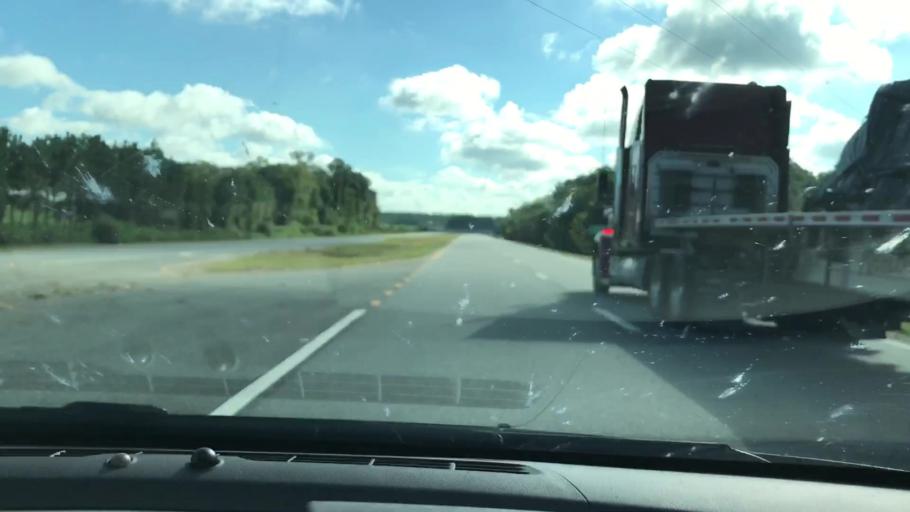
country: US
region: Georgia
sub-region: Worth County
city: Sylvester
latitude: 31.5511
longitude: -83.9578
